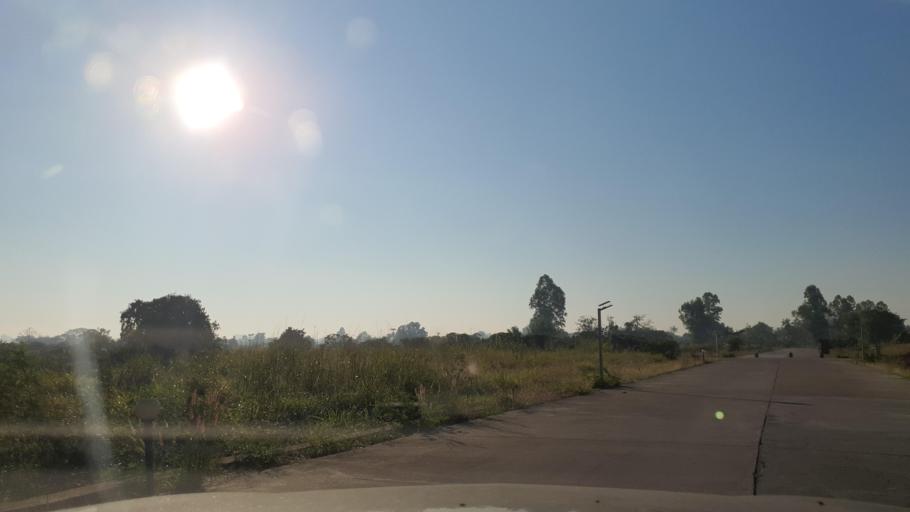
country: TH
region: Chiang Mai
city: Hang Dong
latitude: 18.6961
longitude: 98.9675
